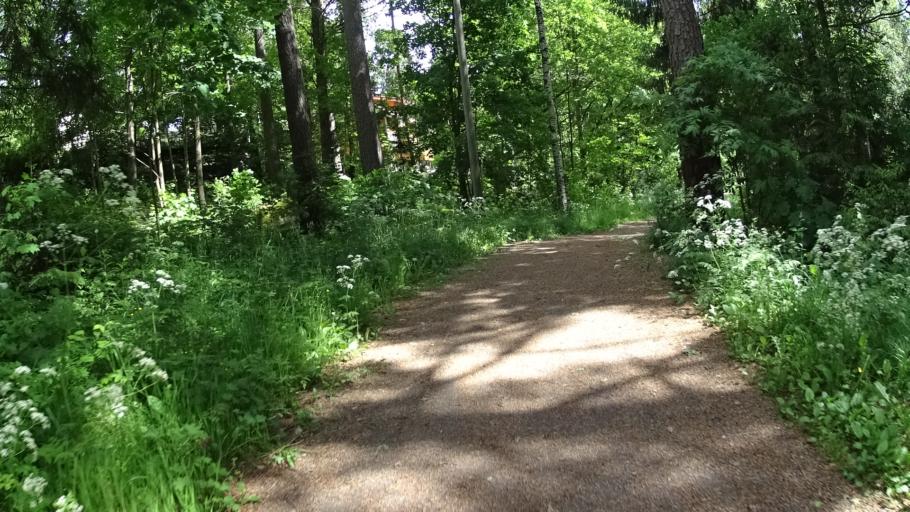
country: FI
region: Uusimaa
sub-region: Helsinki
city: Kauniainen
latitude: 60.2349
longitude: 24.7022
